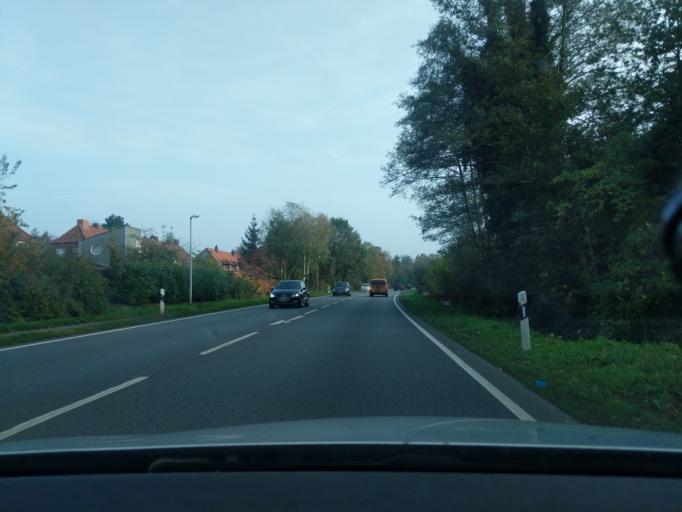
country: DE
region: Lower Saxony
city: Stade
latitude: 53.5893
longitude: 9.4522
